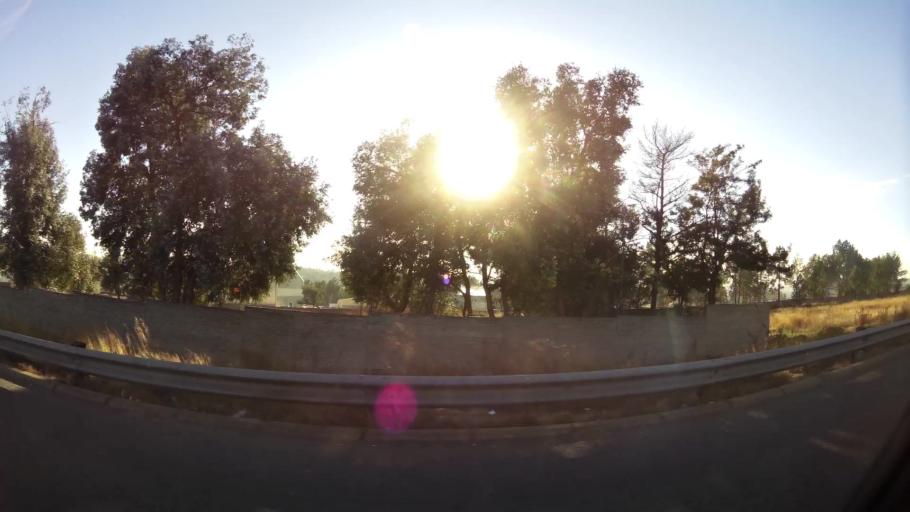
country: ZA
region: Gauteng
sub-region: City of Johannesburg Metropolitan Municipality
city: Midrand
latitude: -26.0342
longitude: 28.1394
